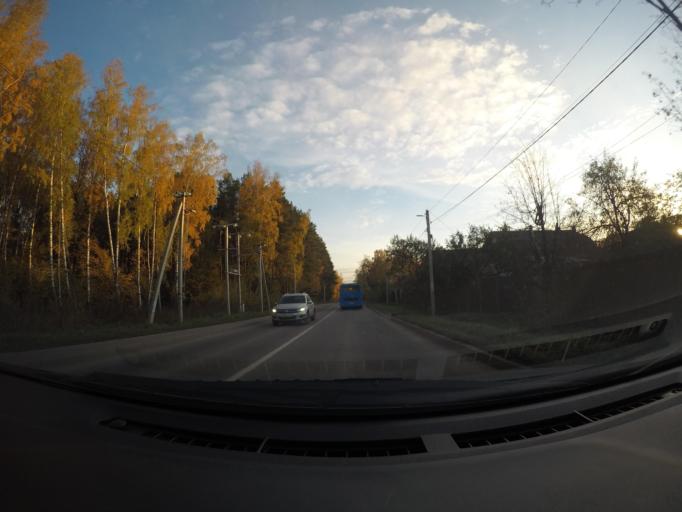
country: RU
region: Moskovskaya
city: Firsanovka
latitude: 55.9423
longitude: 37.2500
